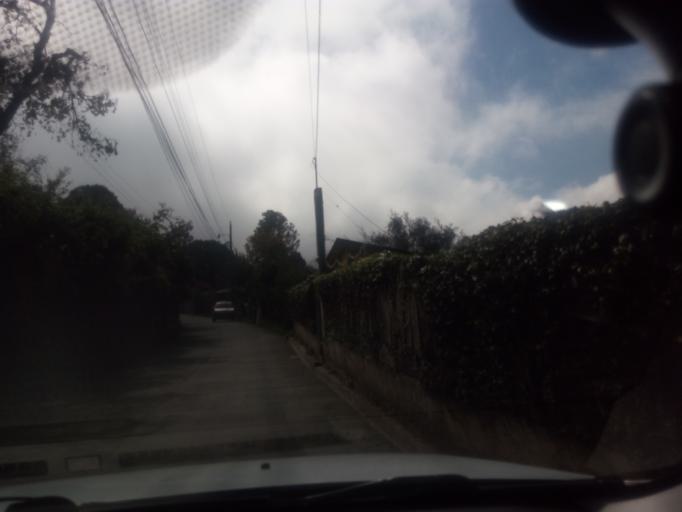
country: GT
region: Sacatepequez
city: San Bartolome Milpas Altas
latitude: 14.6016
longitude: -90.6776
